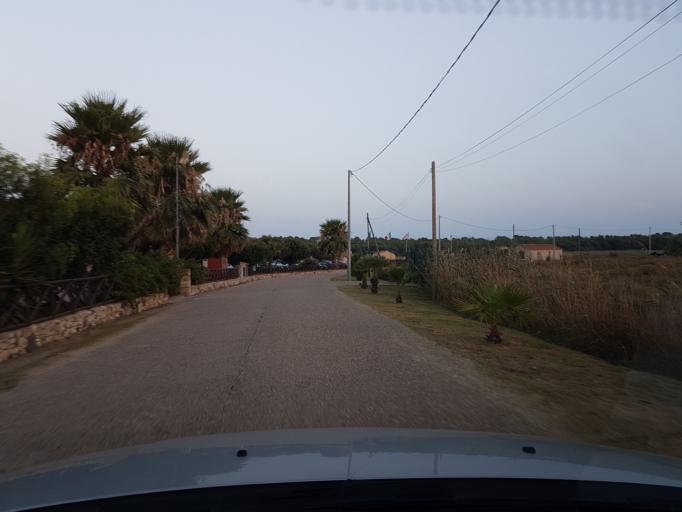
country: IT
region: Sardinia
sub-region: Provincia di Oristano
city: Cabras
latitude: 39.9146
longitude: 8.5088
